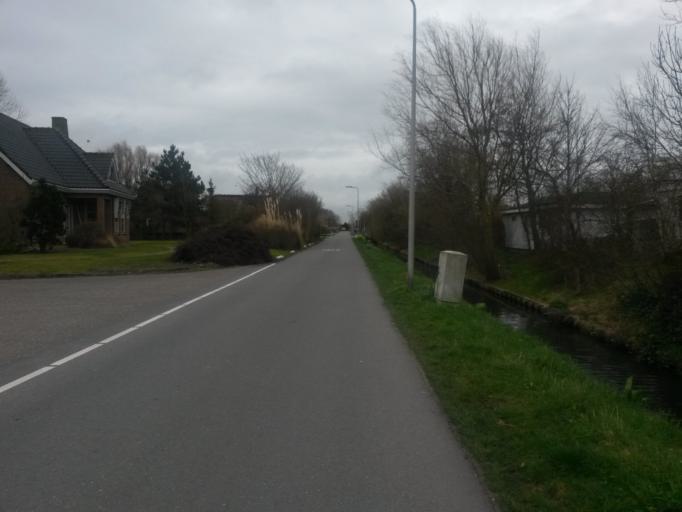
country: NL
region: South Holland
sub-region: Gemeente Rotterdam
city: Hoek van Holland
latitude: 52.0022
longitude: 4.1393
